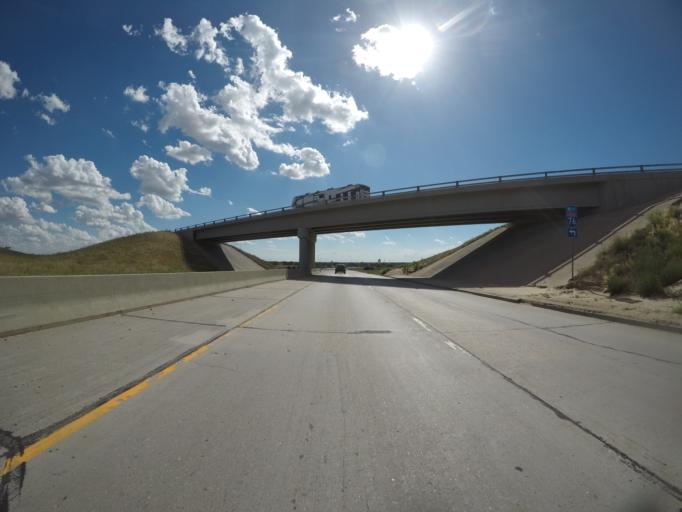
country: US
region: Colorado
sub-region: Logan County
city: Sterling
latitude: 40.6212
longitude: -103.1730
